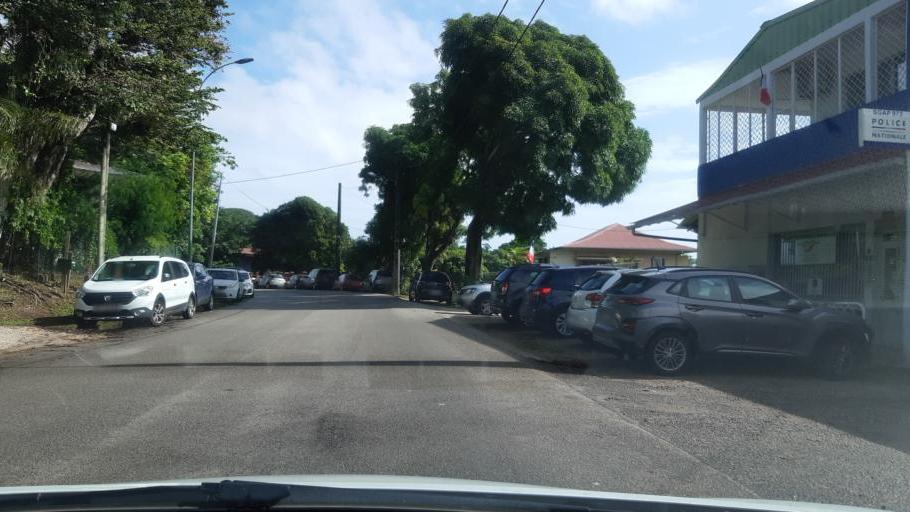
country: GF
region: Guyane
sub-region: Guyane
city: Cayenne
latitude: 4.9396
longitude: -52.3180
